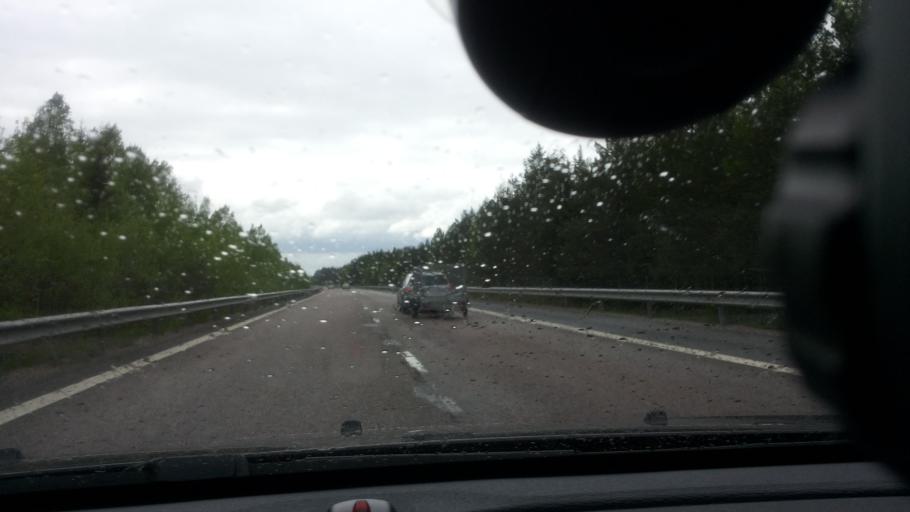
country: SE
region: Uppsala
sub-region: Alvkarleby Kommun
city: AElvkarleby
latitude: 60.4895
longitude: 17.3468
